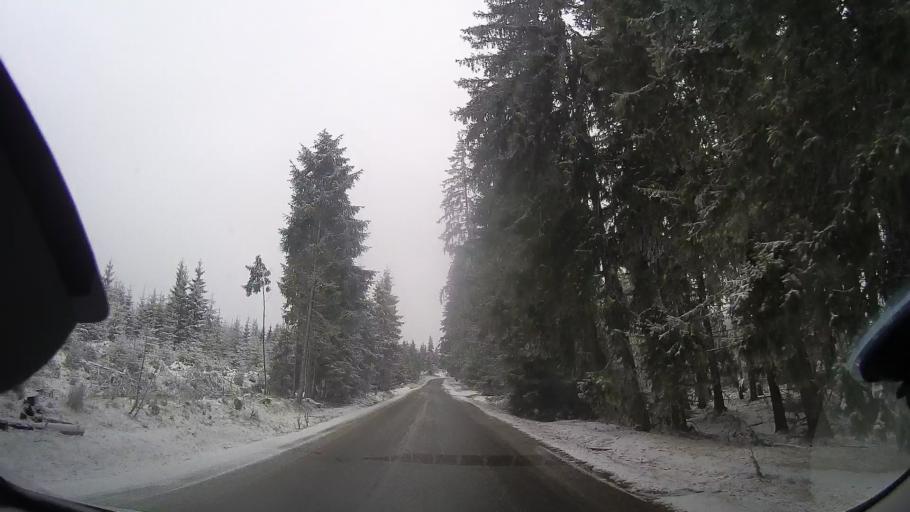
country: RO
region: Cluj
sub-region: Comuna Belis
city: Belis
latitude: 46.6397
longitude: 23.0564
